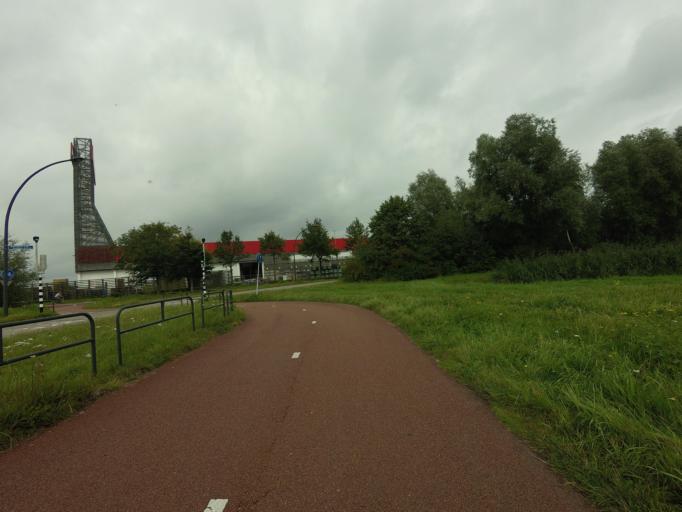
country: NL
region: Overijssel
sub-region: Gemeente Borne
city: Borne
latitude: 52.2857
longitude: 6.7618
